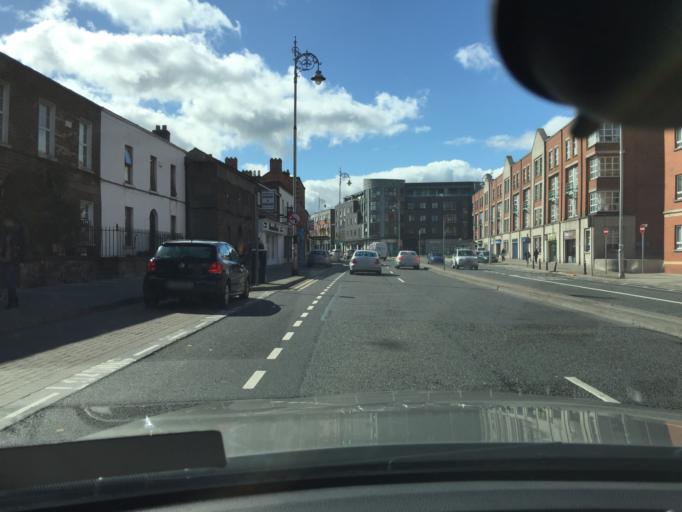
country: IE
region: Leinster
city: Rathmines
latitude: 53.3349
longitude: -6.2740
